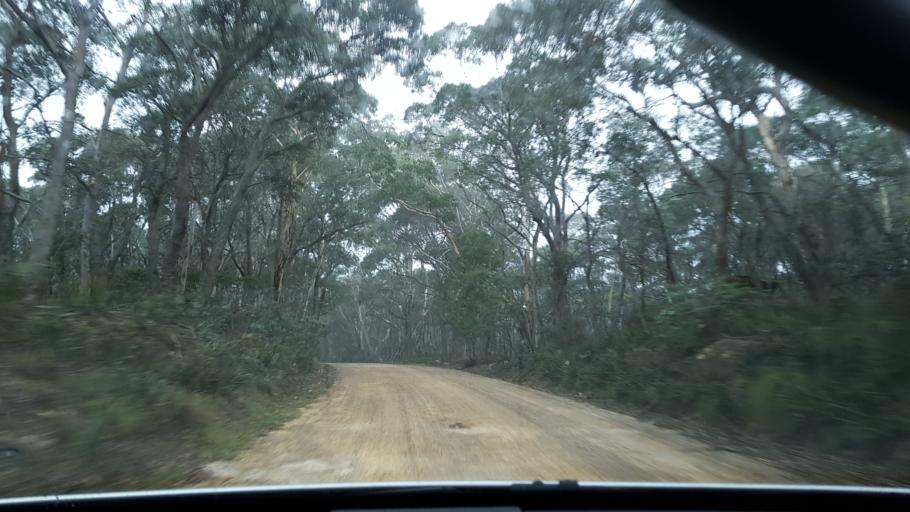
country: AU
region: New South Wales
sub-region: Oberon
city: Oberon
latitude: -33.9877
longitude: 150.0638
